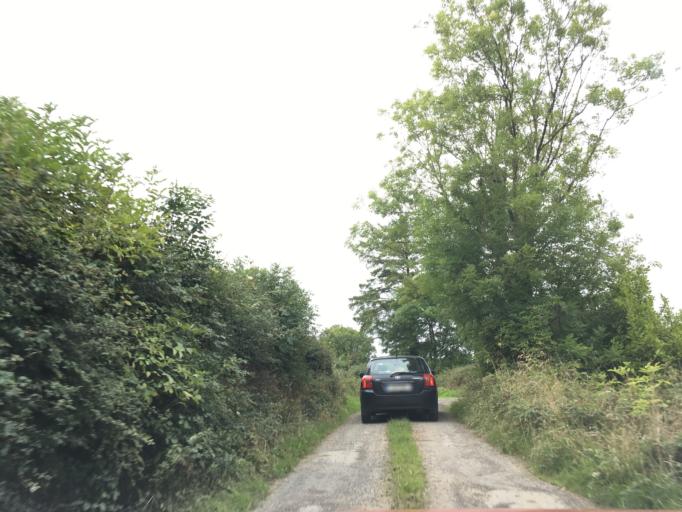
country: IE
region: Munster
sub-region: An Clar
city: Ennis
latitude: 52.7249
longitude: -9.0936
